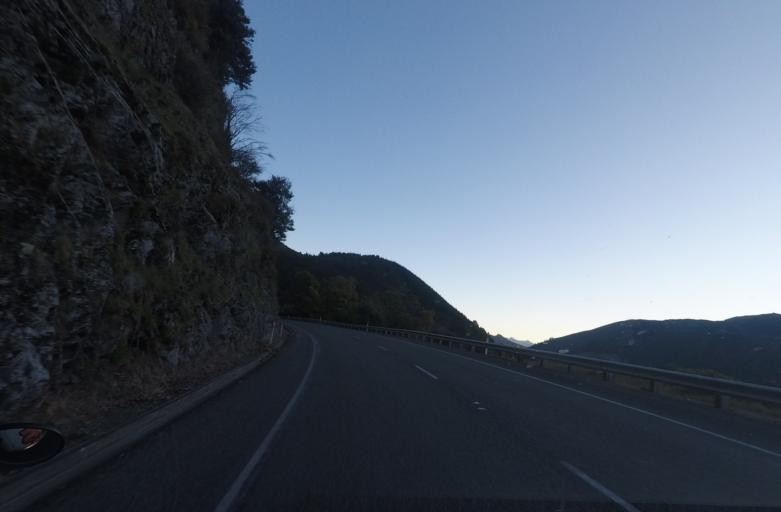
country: NZ
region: Marlborough
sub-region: Marlborough District
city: Picton
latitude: -41.2722
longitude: 173.7459
